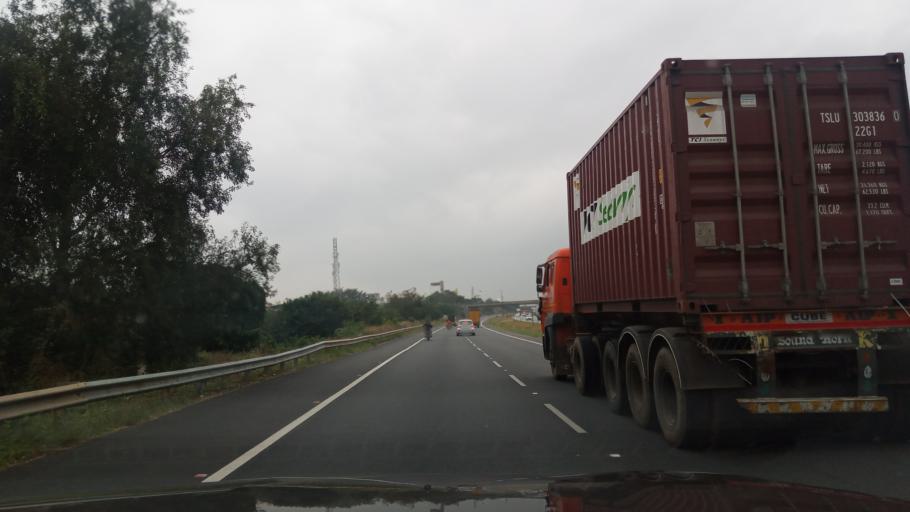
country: IN
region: Karnataka
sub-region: Bangalore Rural
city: Nelamangala
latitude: 13.0166
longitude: 77.4762
